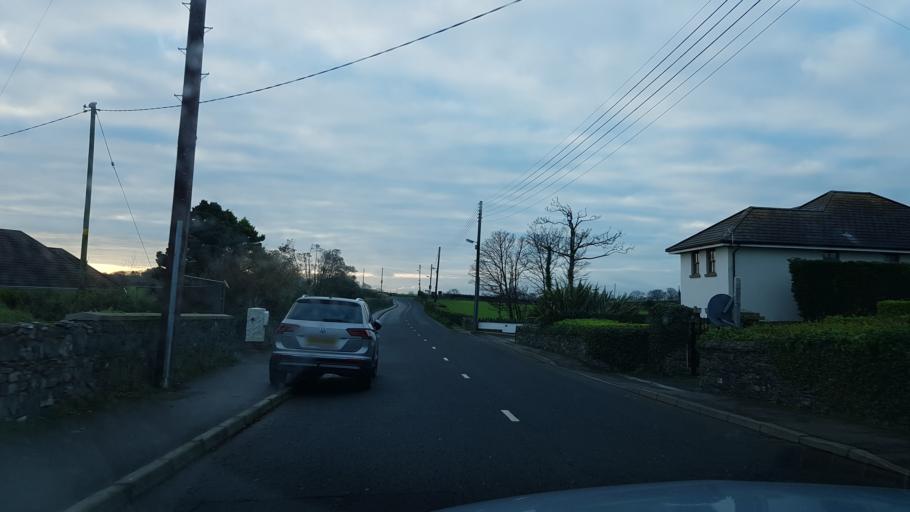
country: GB
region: Northern Ireland
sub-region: North Down District
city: Bangor
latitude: 54.6757
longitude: -5.6229
